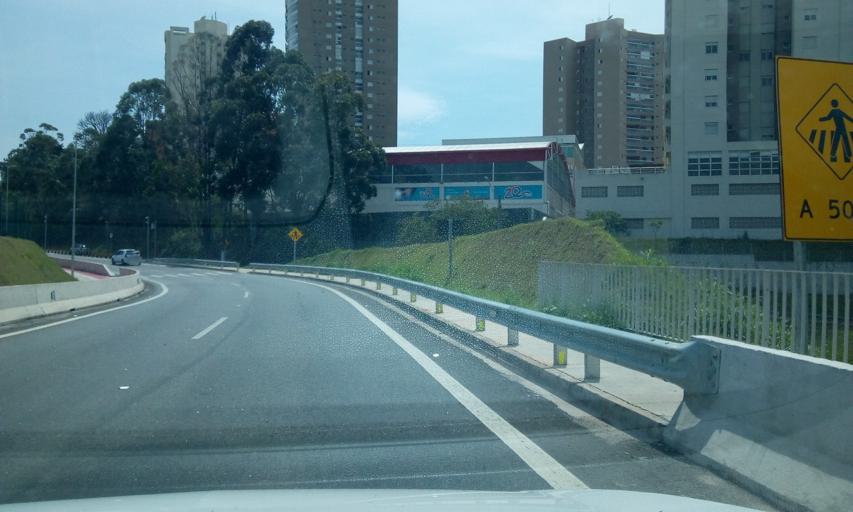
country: BR
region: Sao Paulo
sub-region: Jundiai
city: Jundiai
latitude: -23.2086
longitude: -46.8948
